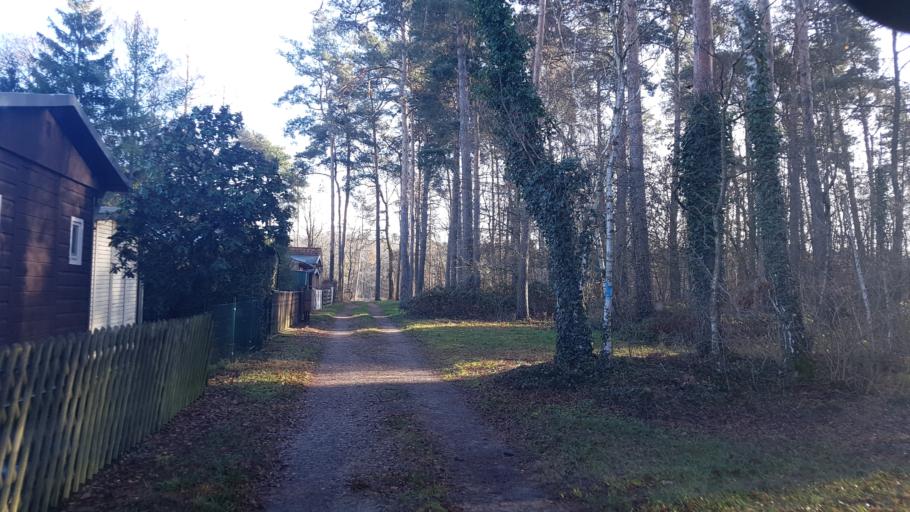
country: DE
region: Brandenburg
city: Ruckersdorf
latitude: 51.5913
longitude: 13.5643
